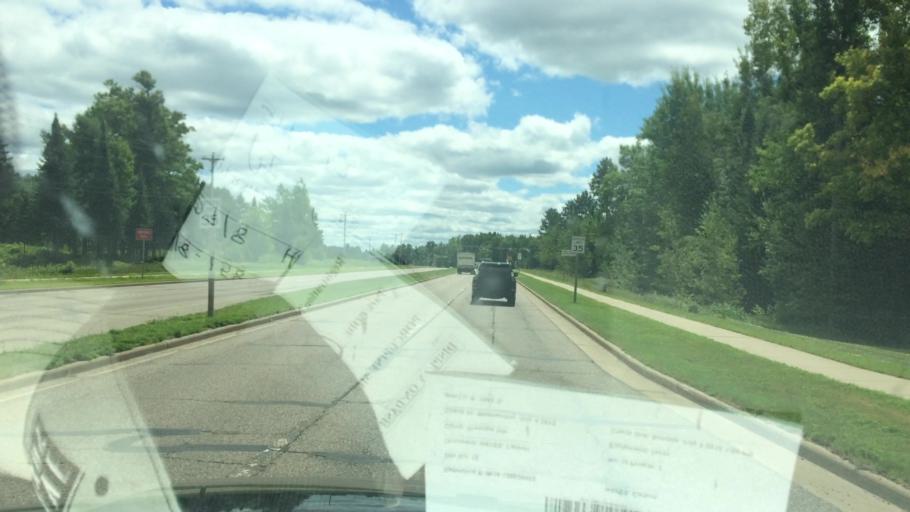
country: US
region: Wisconsin
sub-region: Oneida County
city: Rhinelander
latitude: 45.6477
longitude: -89.3822
